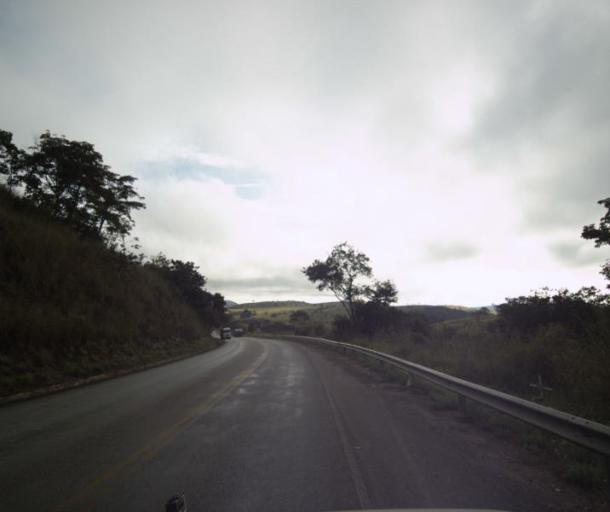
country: BR
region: Goias
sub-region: Pirenopolis
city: Pirenopolis
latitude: -15.7526
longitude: -48.7276
